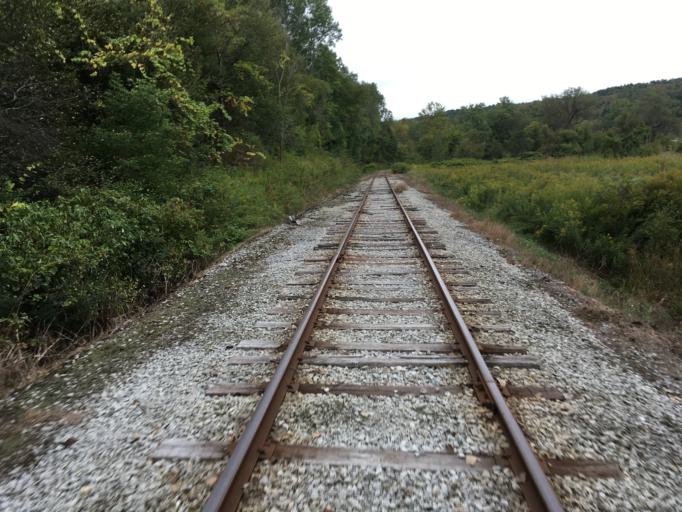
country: US
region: Vermont
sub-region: Washington County
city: Montpelier
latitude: 44.2313
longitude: -72.5497
